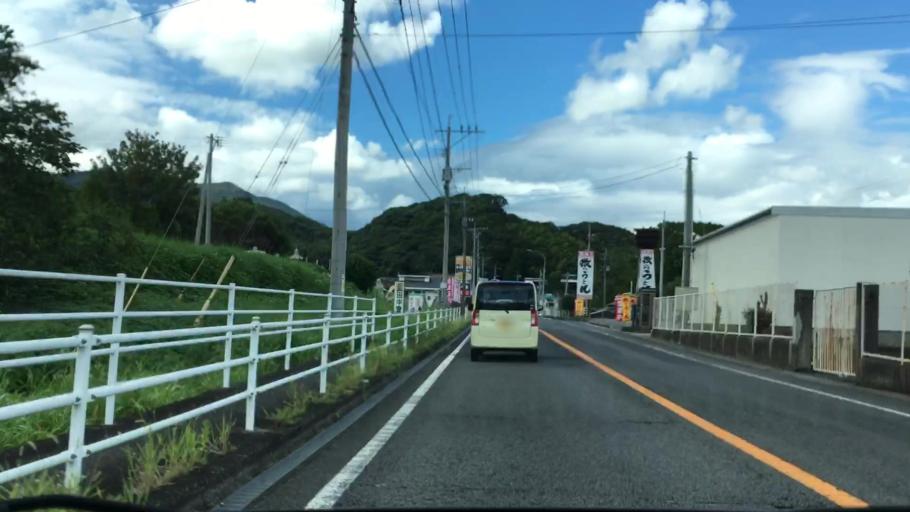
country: JP
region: Nagasaki
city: Sasebo
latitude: 33.1559
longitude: 129.8306
